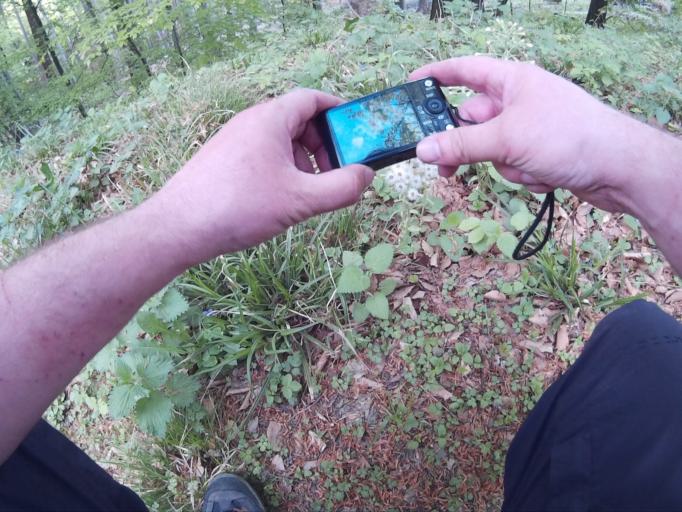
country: AT
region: Burgenland
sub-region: Politischer Bezirk Oberwart
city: Rechnitz
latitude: 47.3535
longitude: 16.4730
